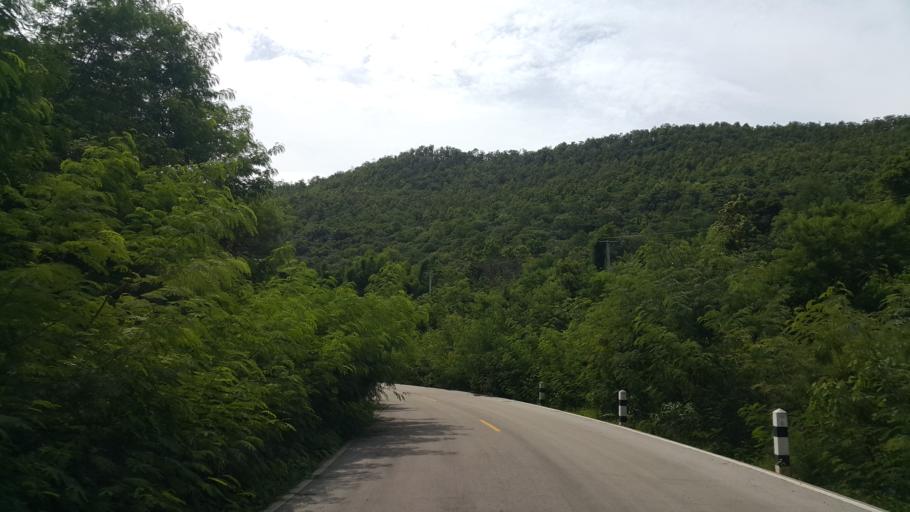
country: TH
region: Chiang Mai
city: Mae On
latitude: 18.7460
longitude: 99.1999
